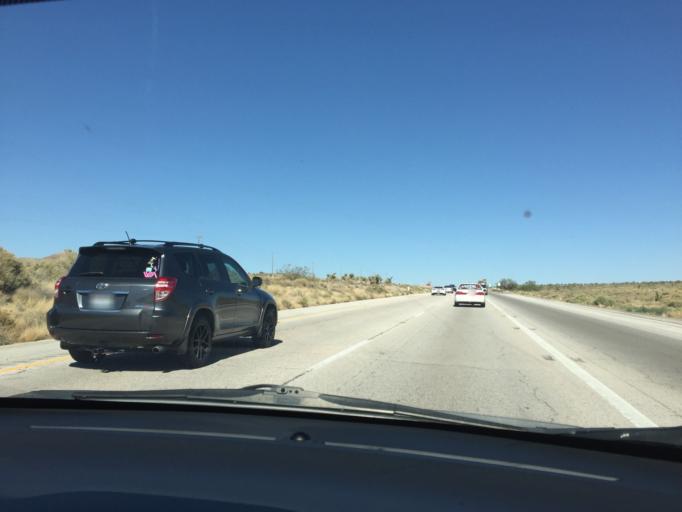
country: US
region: Nevada
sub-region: Clark County
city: Sandy Valley
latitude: 35.4715
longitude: -115.5582
